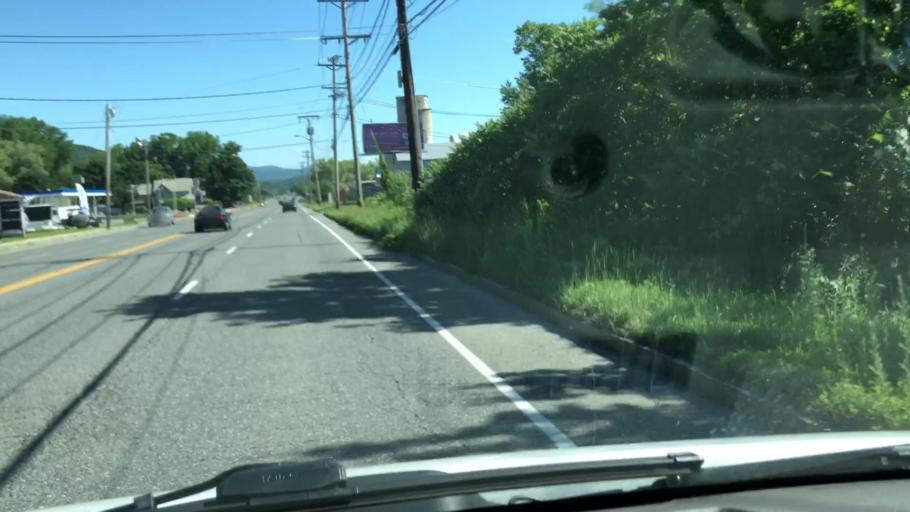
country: US
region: Massachusetts
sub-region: Berkshire County
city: Adams
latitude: 42.6522
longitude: -73.1106
